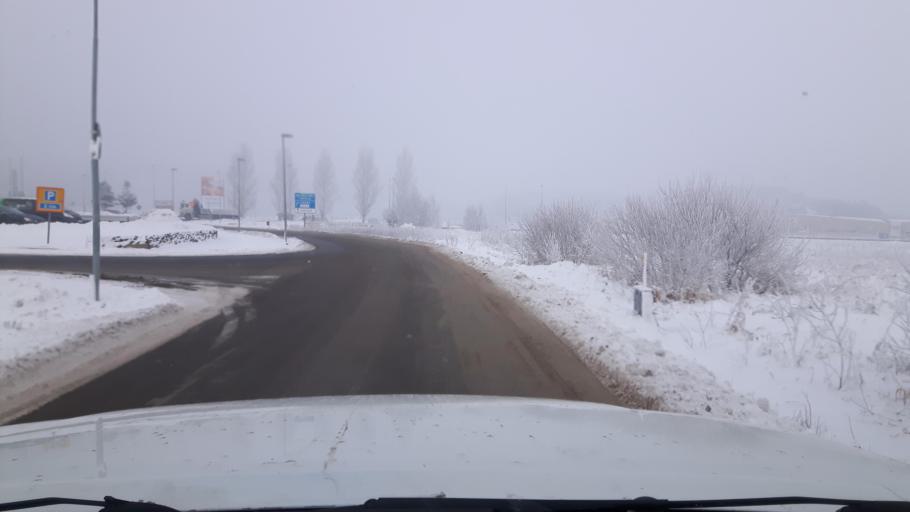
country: SE
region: Halland
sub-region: Kungsbacka Kommun
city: Kungsbacka
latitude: 57.4743
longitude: 12.0610
